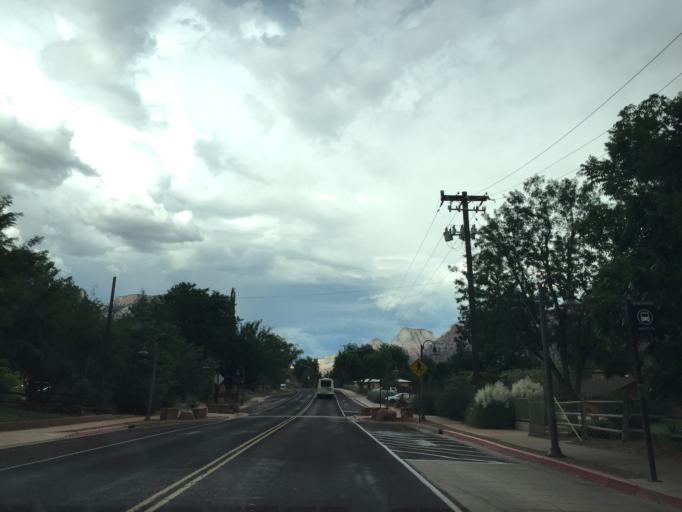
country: US
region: Utah
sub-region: Washington County
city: Hildale
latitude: 37.1793
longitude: -113.0072
